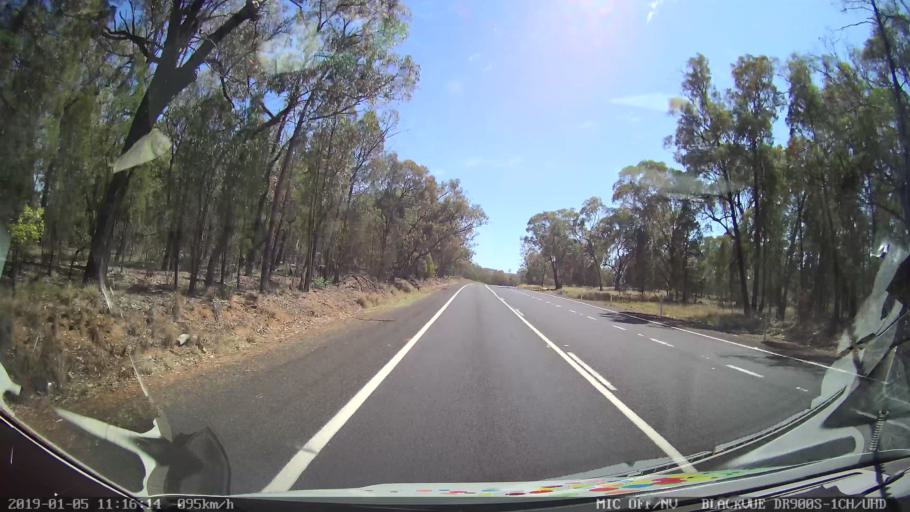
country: AU
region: New South Wales
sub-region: Warrumbungle Shire
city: Coonabarabran
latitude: -31.3416
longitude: 149.2972
